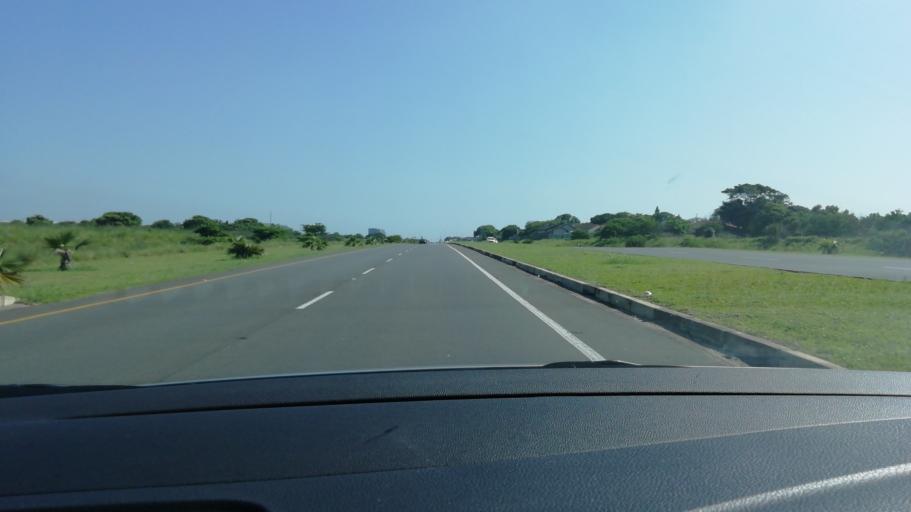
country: ZA
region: KwaZulu-Natal
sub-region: uThungulu District Municipality
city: Richards Bay
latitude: -28.7647
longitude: 32.0488
